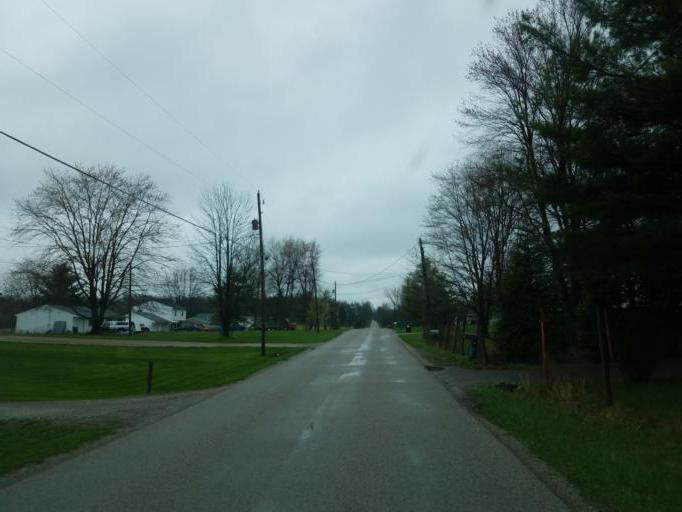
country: US
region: Ohio
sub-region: Morrow County
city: Mount Gilead
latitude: 40.4545
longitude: -82.8071
